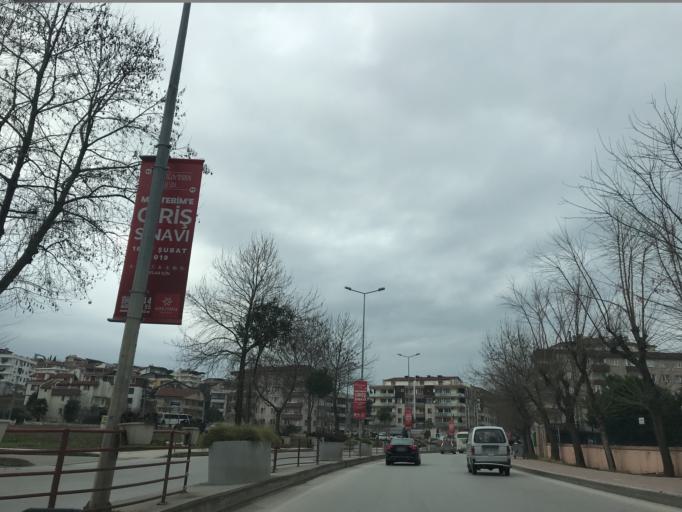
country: TR
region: Yalova
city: Yalova
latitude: 40.6516
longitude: 29.2596
